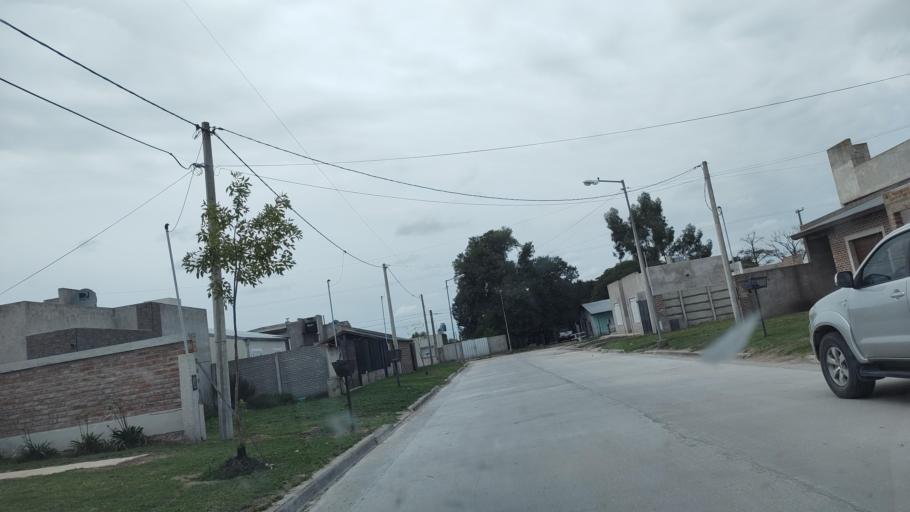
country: AR
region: Buenos Aires
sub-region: Partido de Loberia
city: Loberia
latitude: -38.1619
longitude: -58.7729
